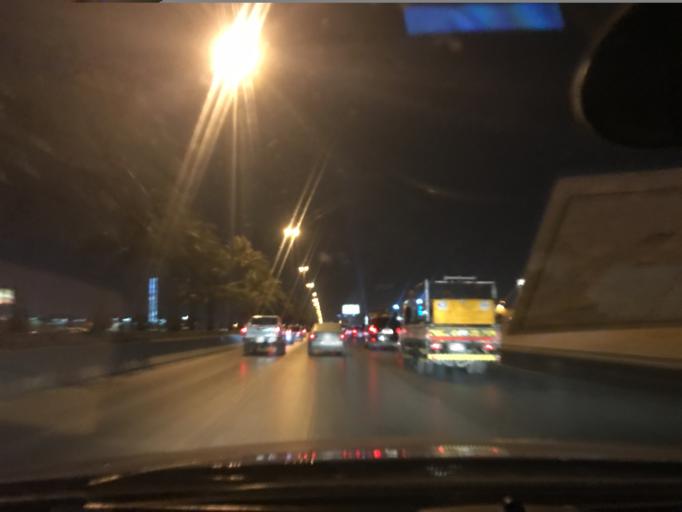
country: SA
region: Ar Riyad
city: Riyadh
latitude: 24.7606
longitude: 46.7386
